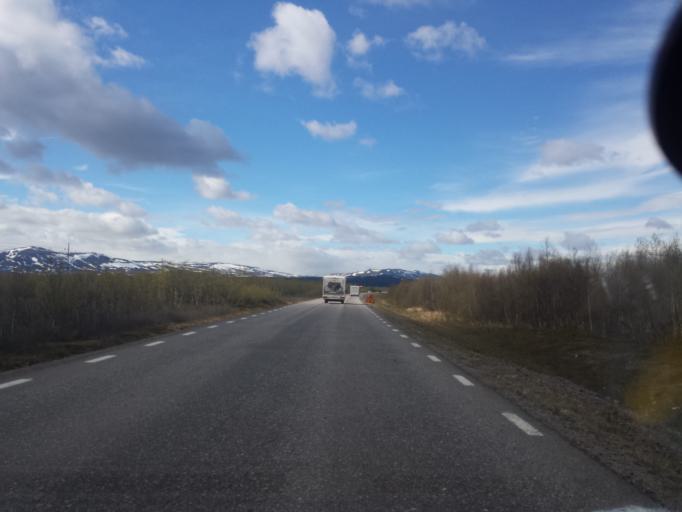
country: SE
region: Norrbotten
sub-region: Kiruna Kommun
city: Kiruna
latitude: 68.0039
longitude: 19.8542
